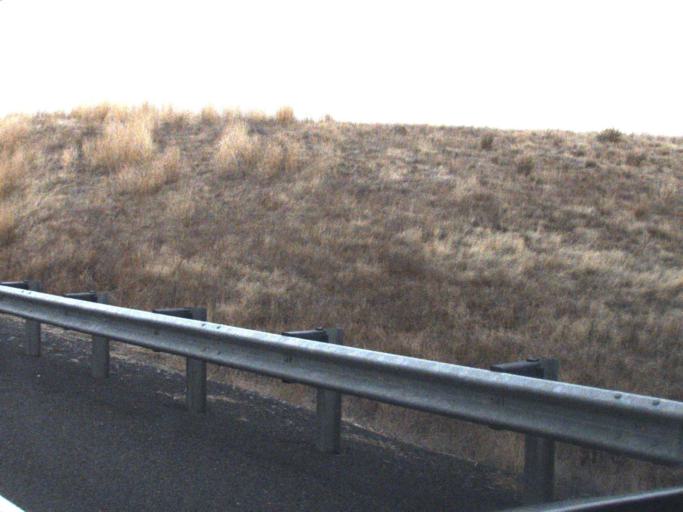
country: US
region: Washington
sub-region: Adams County
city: Ritzville
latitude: 46.7721
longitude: -118.3552
